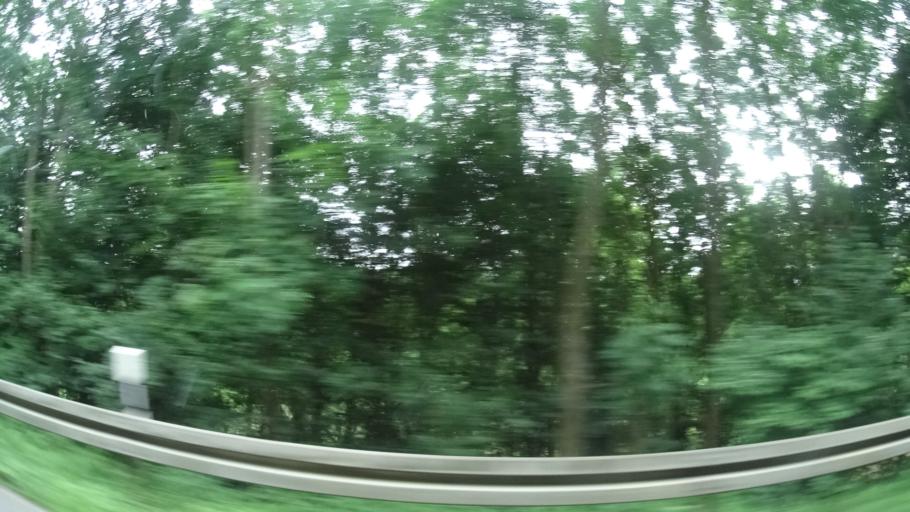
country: DE
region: North Rhine-Westphalia
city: Brakel
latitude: 51.6410
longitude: 9.1366
